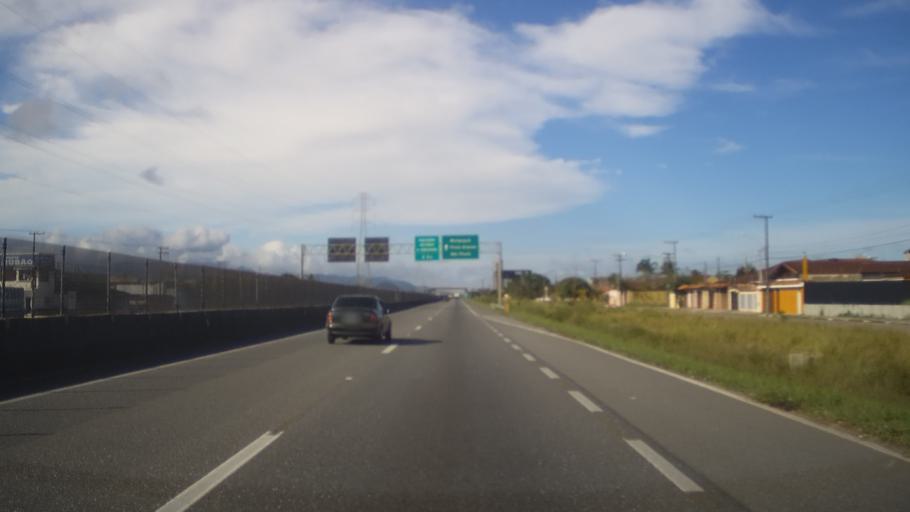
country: BR
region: Sao Paulo
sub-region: Itanhaem
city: Itanhaem
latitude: -24.1506
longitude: -46.7323
